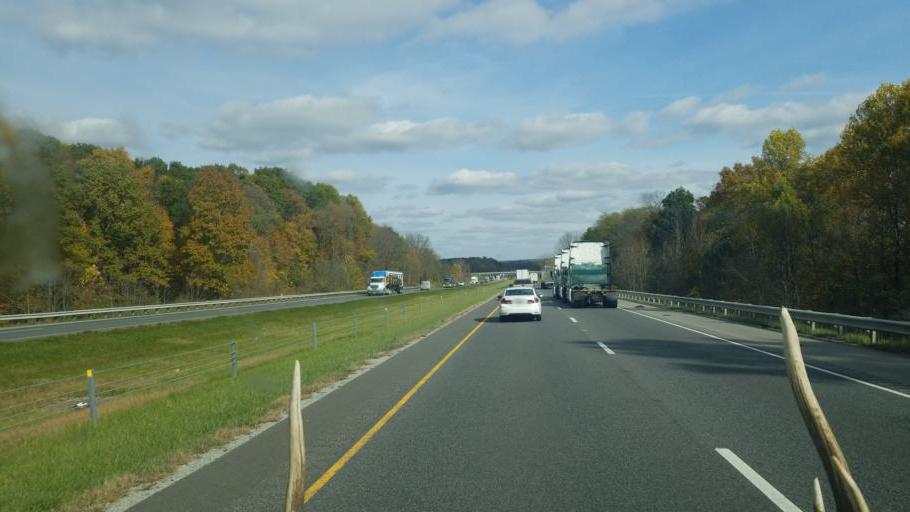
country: US
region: Indiana
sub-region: Henry County
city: Knightstown
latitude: 39.8462
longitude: -85.5029
